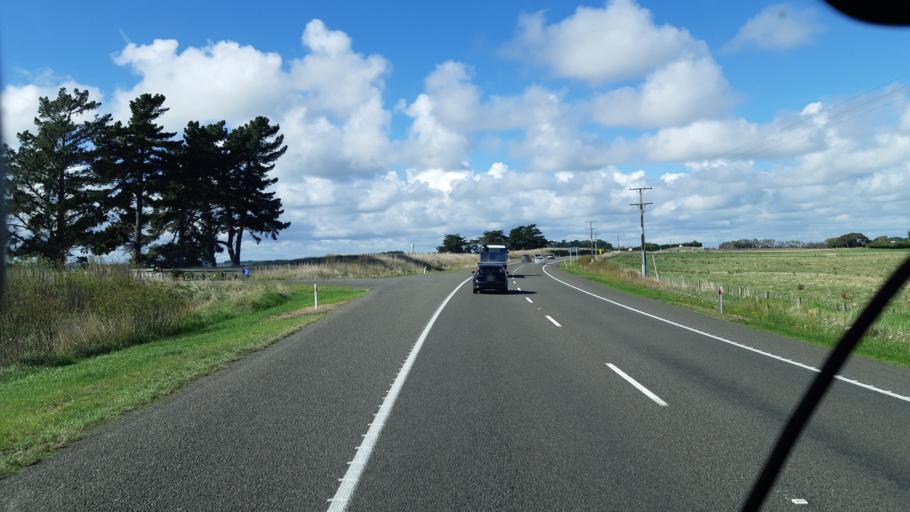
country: NZ
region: Manawatu-Wanganui
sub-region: Wanganui District
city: Wanganui
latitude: -39.9748
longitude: 175.1258
